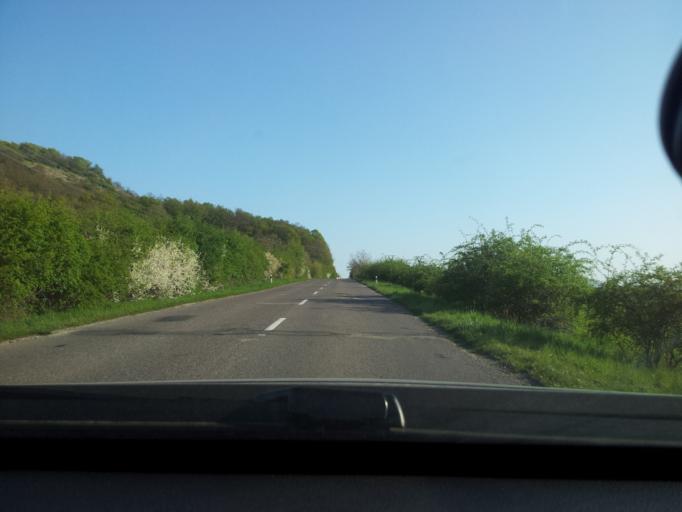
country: SK
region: Nitriansky
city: Tlmace
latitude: 48.2728
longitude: 18.4468
